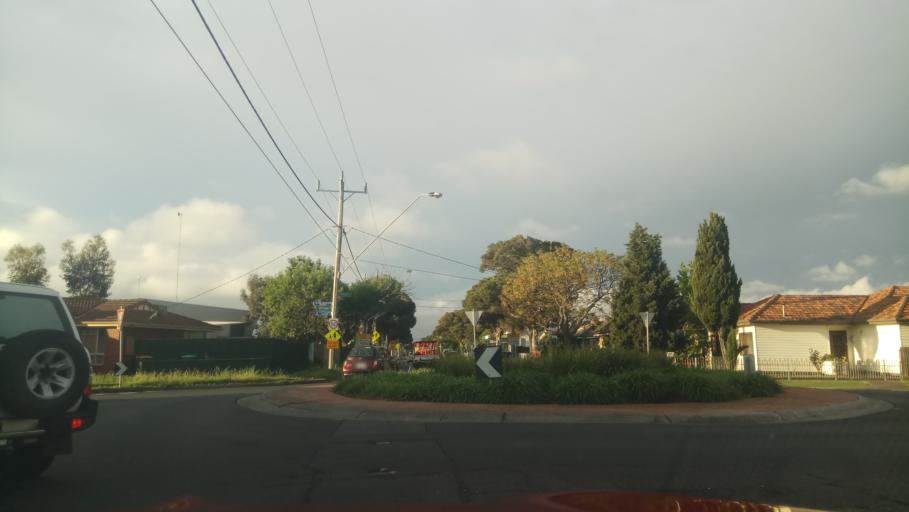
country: AU
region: Victoria
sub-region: Hobsons Bay
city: Williamstown North
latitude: -37.8473
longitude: 144.8686
